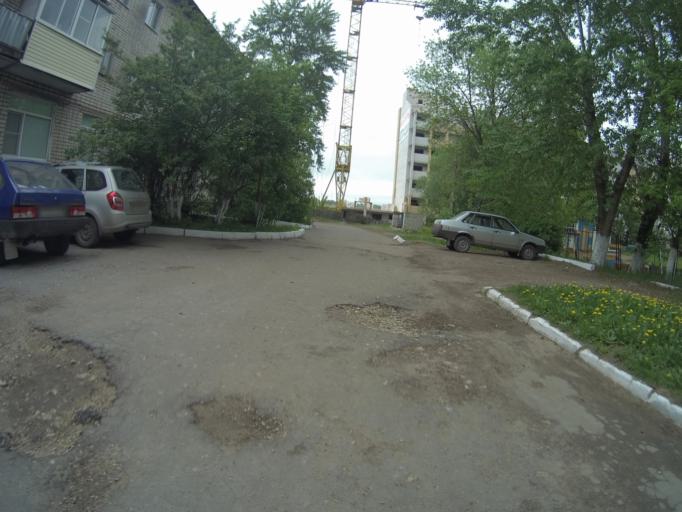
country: RU
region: Vladimir
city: Kommunar
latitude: 56.1117
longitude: 40.4326
